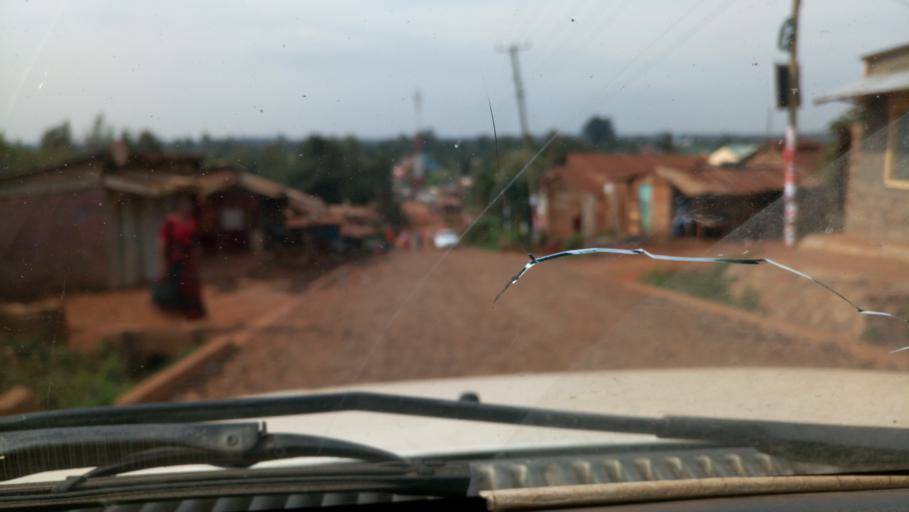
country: KE
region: Kiambu
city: Kikuyu
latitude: -1.2656
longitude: 36.7050
